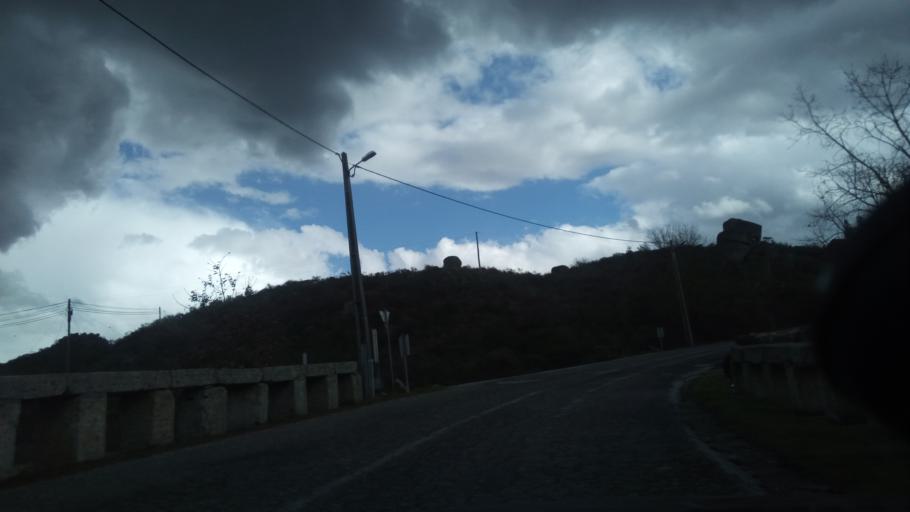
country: PT
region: Guarda
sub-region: Celorico da Beira
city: Celorico da Beira
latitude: 40.6286
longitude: -7.4332
